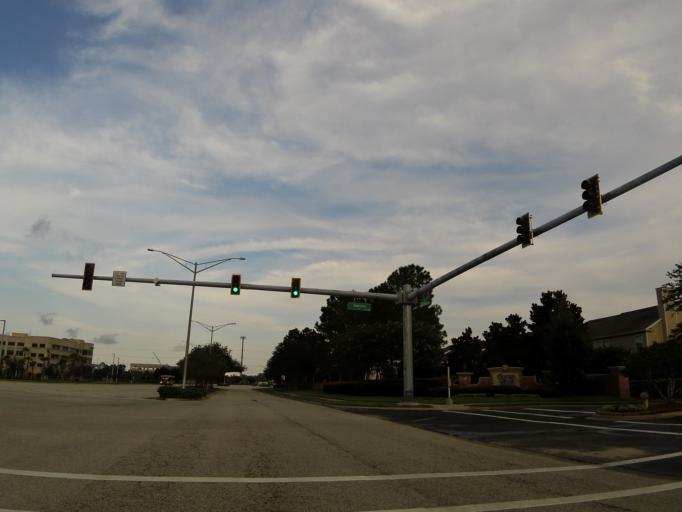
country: US
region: Florida
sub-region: Saint Johns County
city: Ponte Vedra Beach
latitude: 30.2479
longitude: -81.5258
